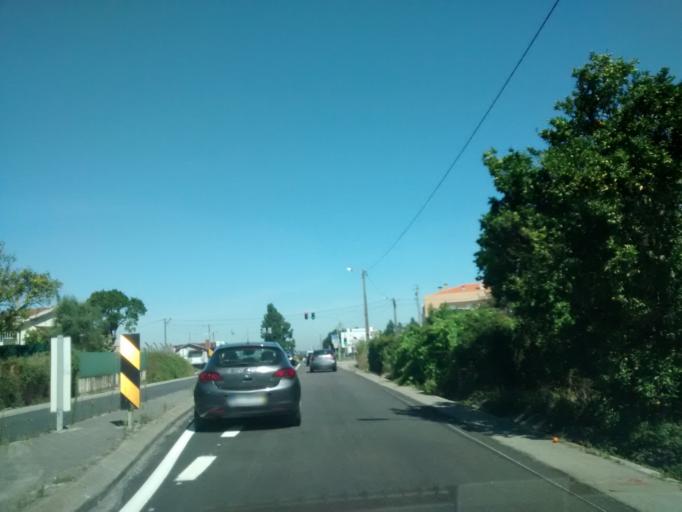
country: PT
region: Aveiro
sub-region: Oliveira do Bairro
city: Oia
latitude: 40.5424
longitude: -8.5323
